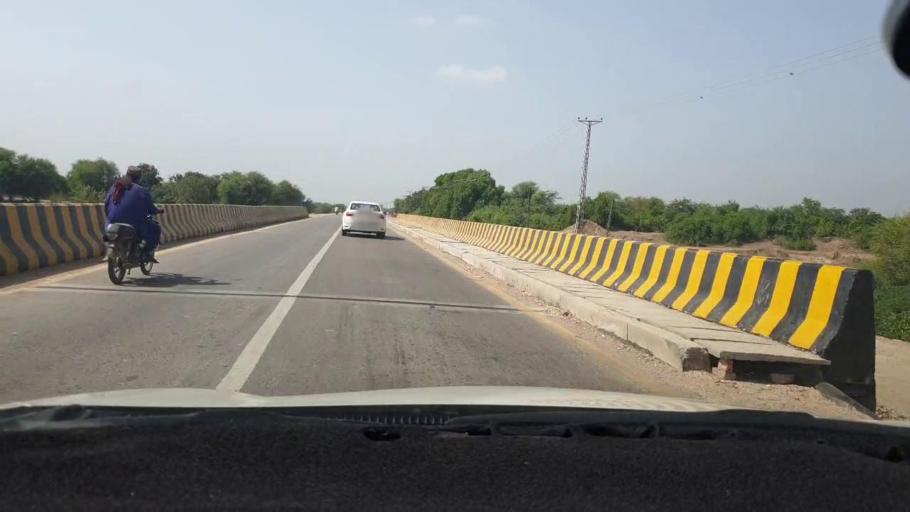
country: PK
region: Sindh
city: Mirpur Khas
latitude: 25.6969
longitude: 69.1207
